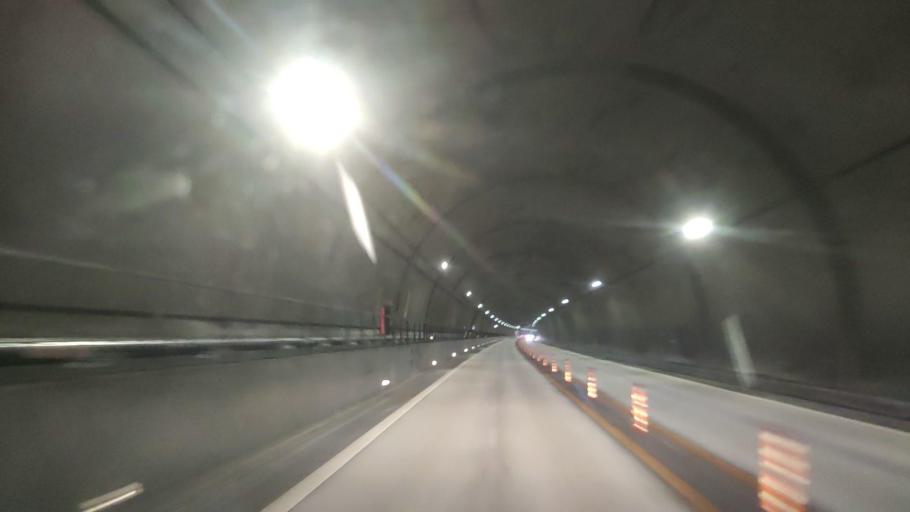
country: JP
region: Ehime
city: Hojo
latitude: 34.0803
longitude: 132.9765
